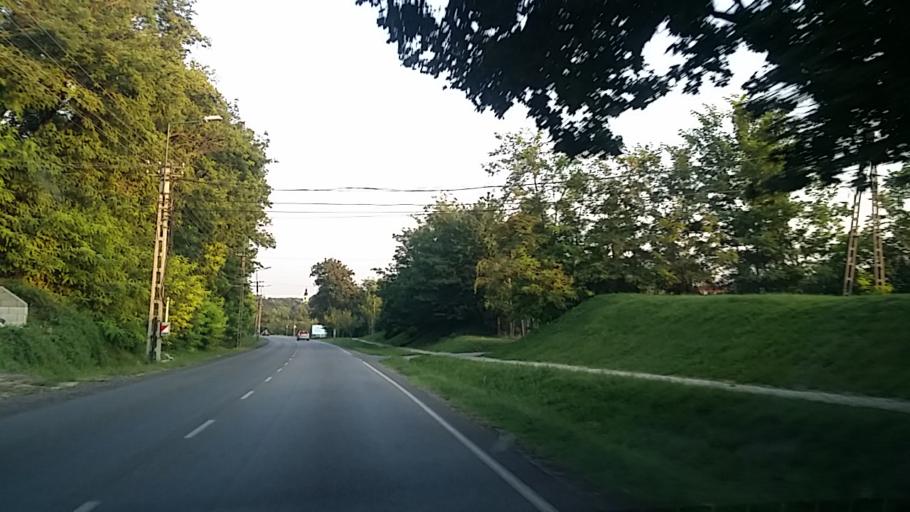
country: HU
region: Fejer
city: dunaujvaros
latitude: 46.9874
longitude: 18.9316
